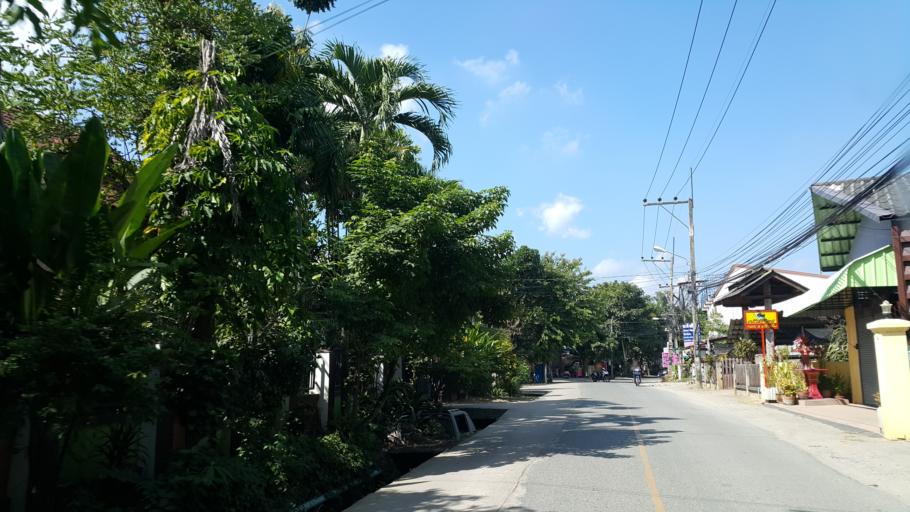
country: TH
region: Chiang Mai
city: San Sai
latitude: 18.8357
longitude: 99.0189
